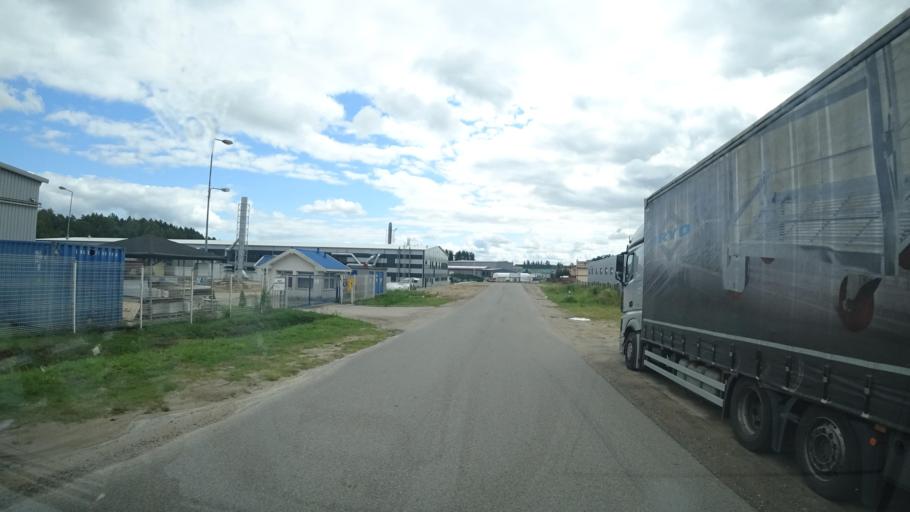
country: PL
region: Warmian-Masurian Voivodeship
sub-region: Powiat goldapski
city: Goldap
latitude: 54.3357
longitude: 22.2928
